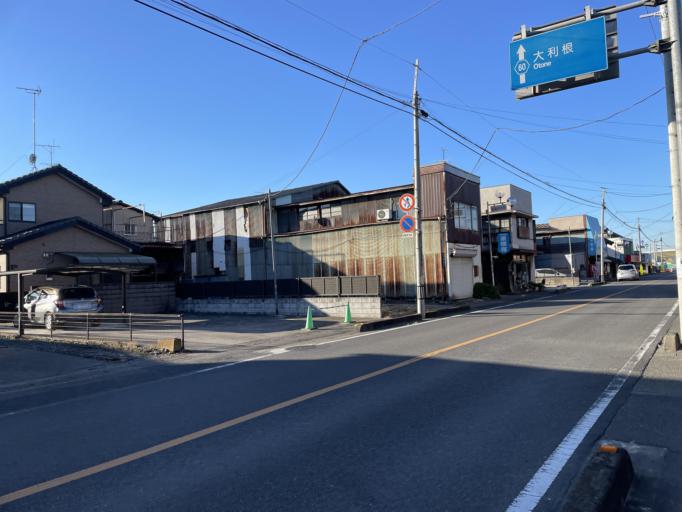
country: JP
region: Saitama
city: Kurihashi
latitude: 36.1403
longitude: 139.7031
